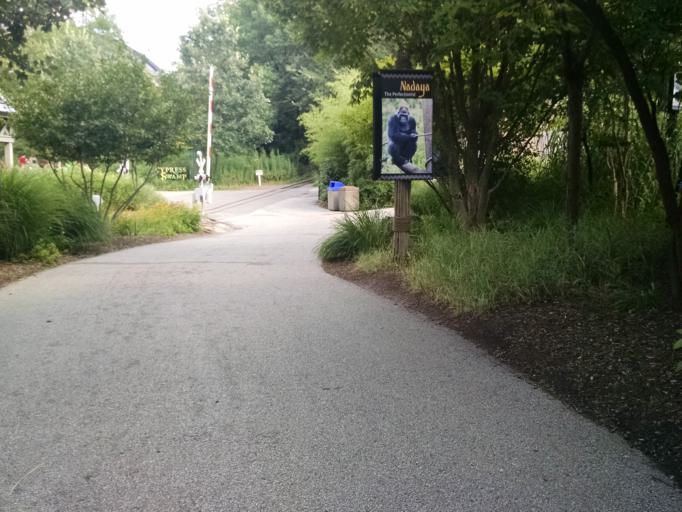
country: US
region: Missouri
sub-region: Saint Louis County
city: University City
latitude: 38.6360
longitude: -90.2886
